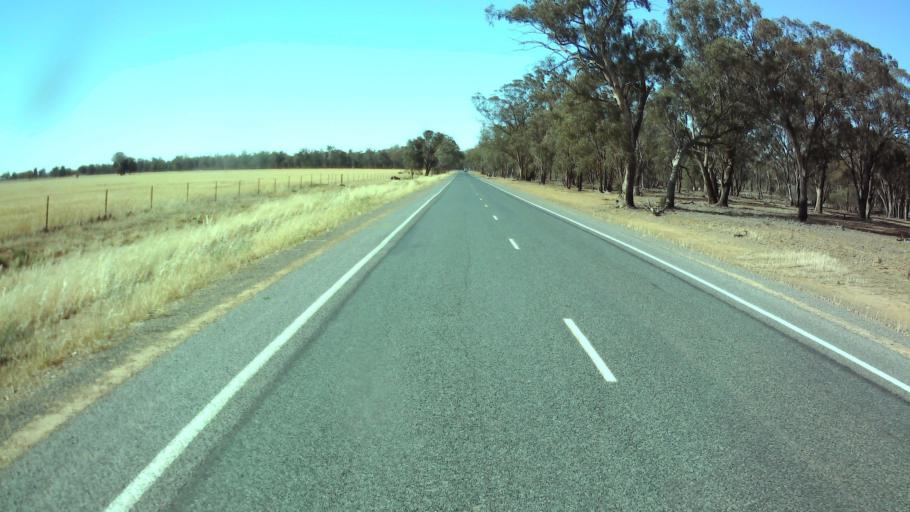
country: AU
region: New South Wales
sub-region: Weddin
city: Grenfell
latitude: -33.7364
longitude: 148.0887
